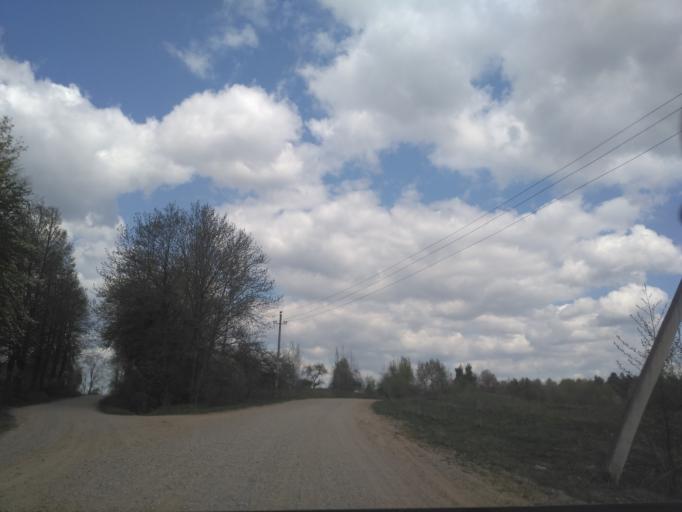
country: BY
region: Minsk
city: Radashkovichy
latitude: 54.2744
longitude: 27.3108
